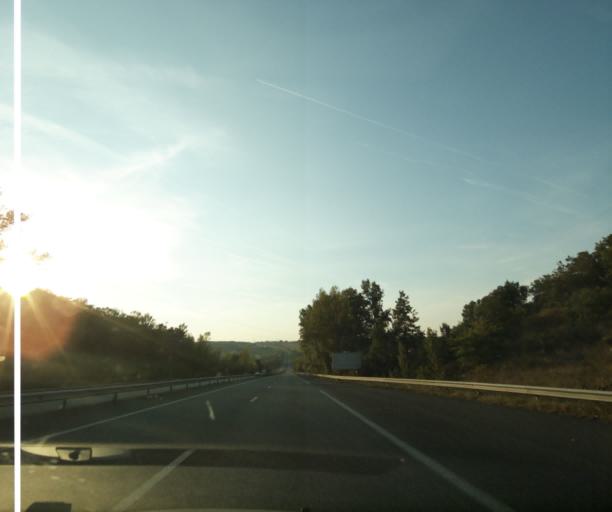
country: FR
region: Midi-Pyrenees
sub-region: Departement du Tarn-et-Garonne
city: Auvillar
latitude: 44.0582
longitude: 0.8719
